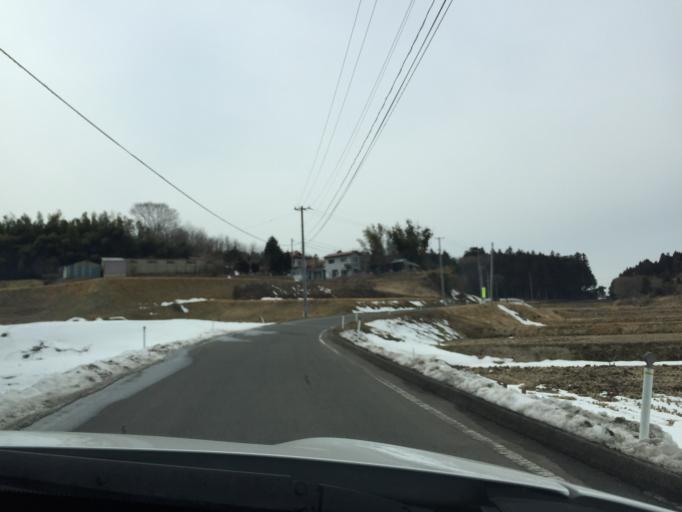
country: JP
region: Fukushima
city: Ishikawa
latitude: 37.1975
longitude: 140.5708
